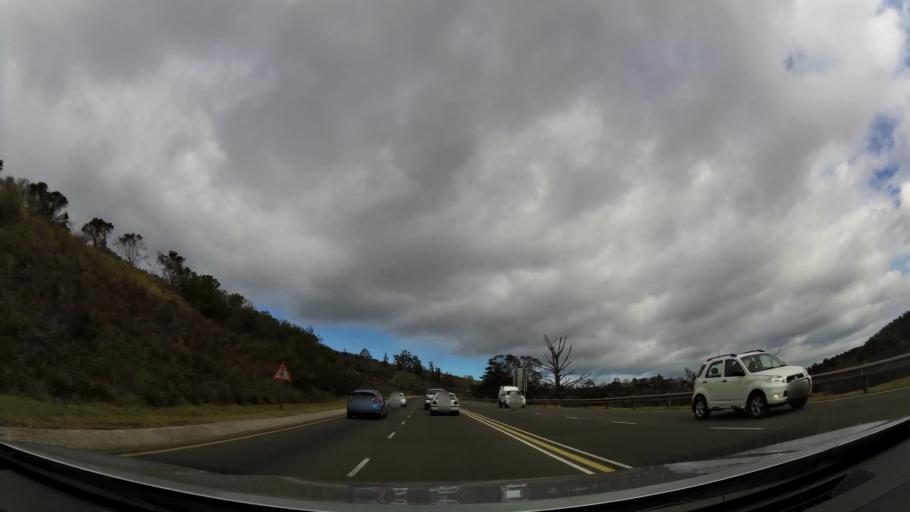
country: ZA
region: Western Cape
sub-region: Eden District Municipality
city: George
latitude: -33.9881
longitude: 22.5402
